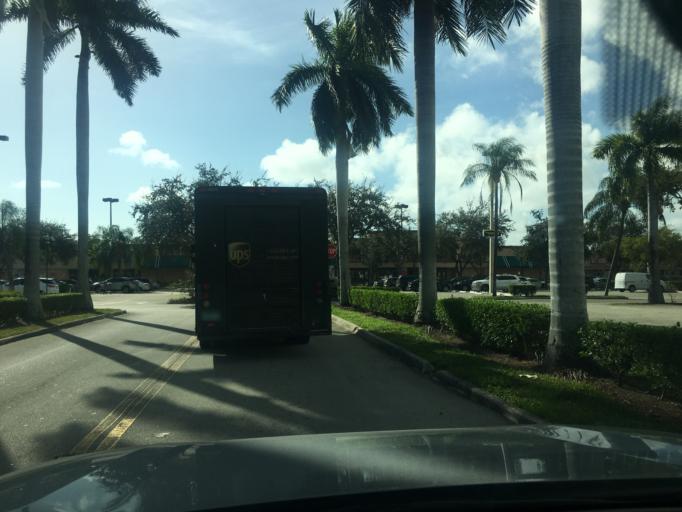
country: US
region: Florida
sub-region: Broward County
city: Pembroke Park
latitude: 25.9847
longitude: -80.1635
